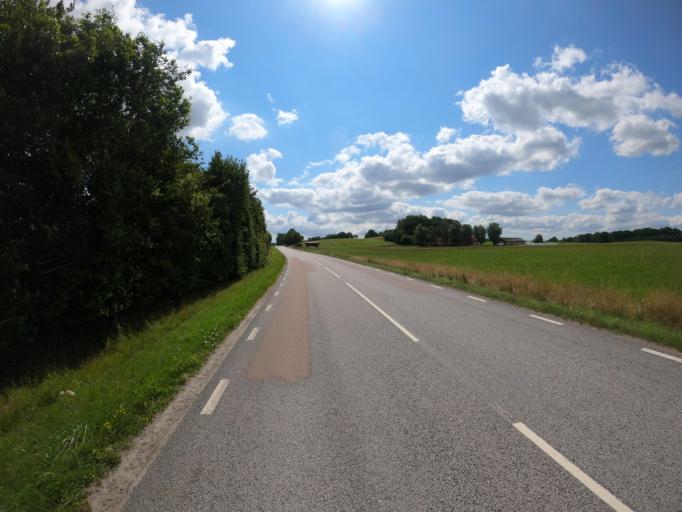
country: SE
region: Skane
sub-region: Lunds Kommun
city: Veberod
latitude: 55.6070
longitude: 13.4876
